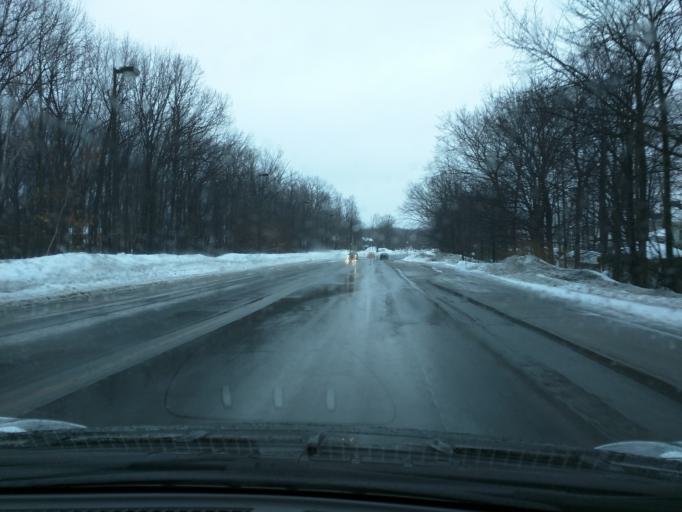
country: CA
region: Quebec
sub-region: Monteregie
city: Longueuil
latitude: 45.5482
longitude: -73.4808
